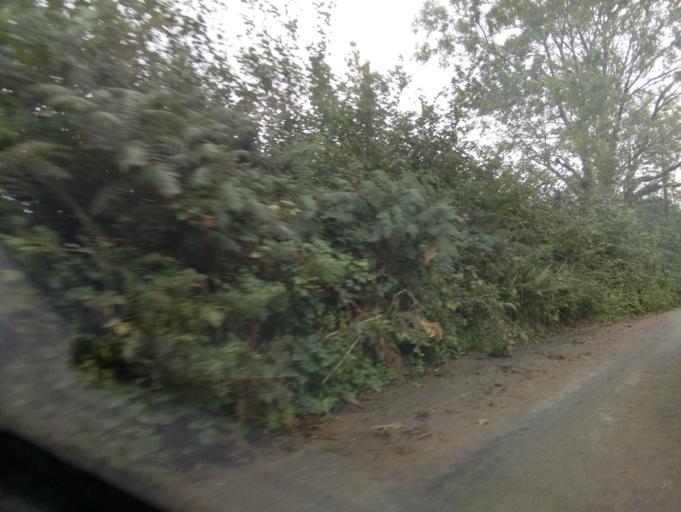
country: GB
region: England
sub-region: Devon
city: Totnes
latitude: 50.3404
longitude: -3.6848
